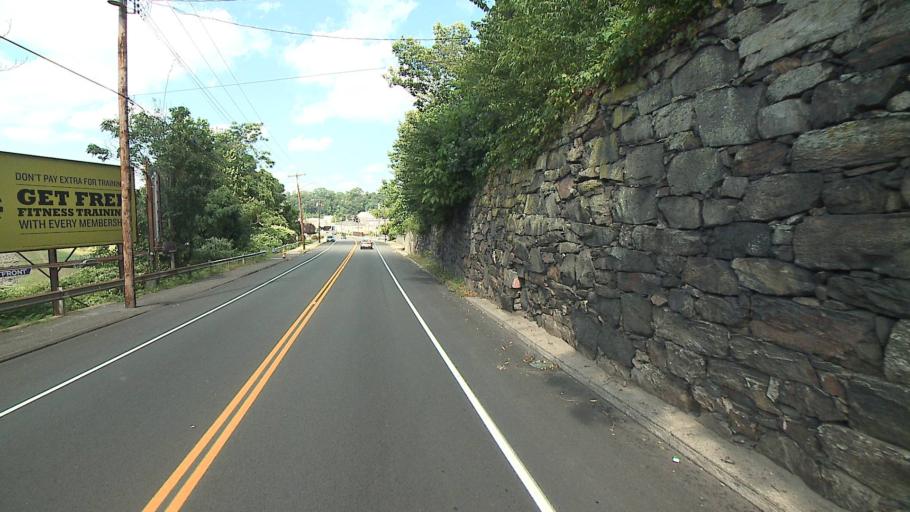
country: US
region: Connecticut
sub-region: New Haven County
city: Ansonia
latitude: 41.3338
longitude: -73.0764
